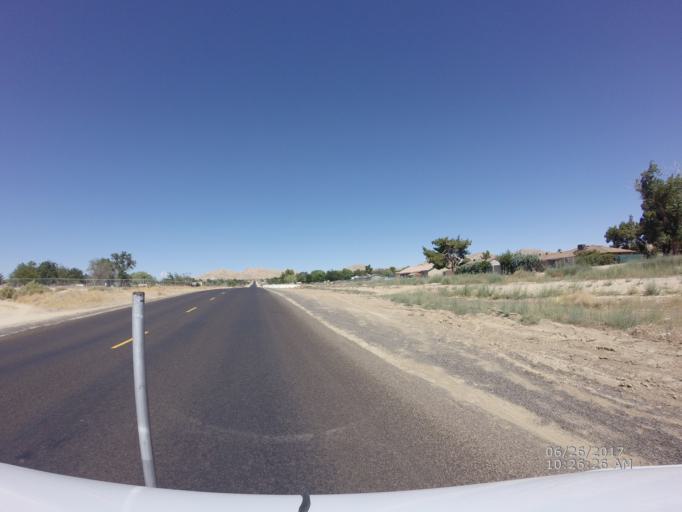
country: US
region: California
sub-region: Los Angeles County
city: Lake Los Angeles
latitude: 34.5946
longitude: -117.8276
